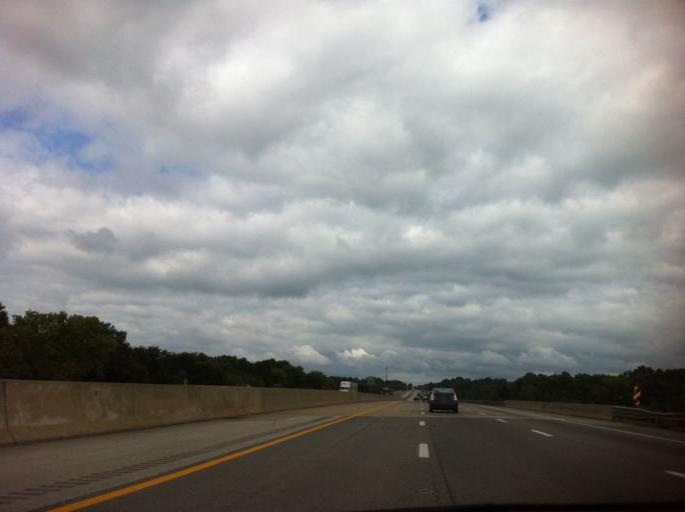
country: US
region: Ohio
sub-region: Trumbull County
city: Newton Falls
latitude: 41.2233
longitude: -80.9613
